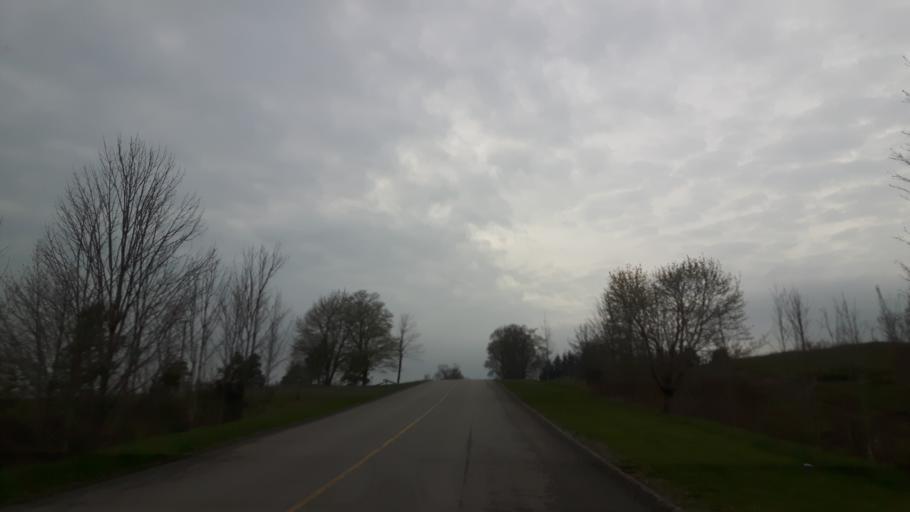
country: CA
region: Ontario
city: Bluewater
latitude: 43.5125
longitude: -81.6692
